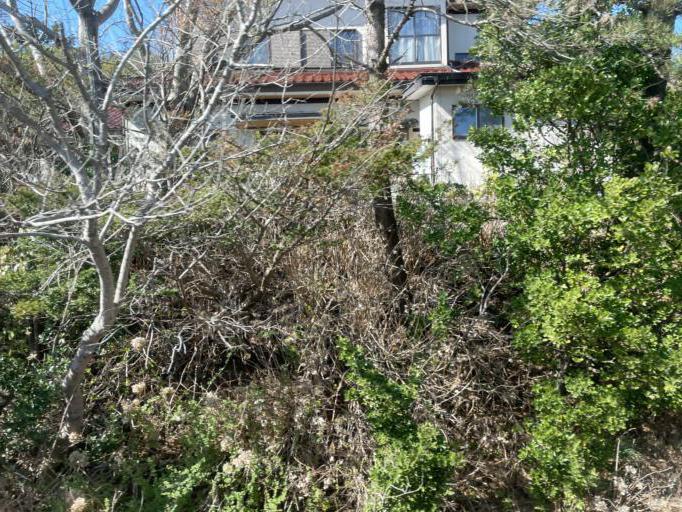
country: JP
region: Aomori
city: Hachinohe
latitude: 40.3440
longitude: 141.7700
